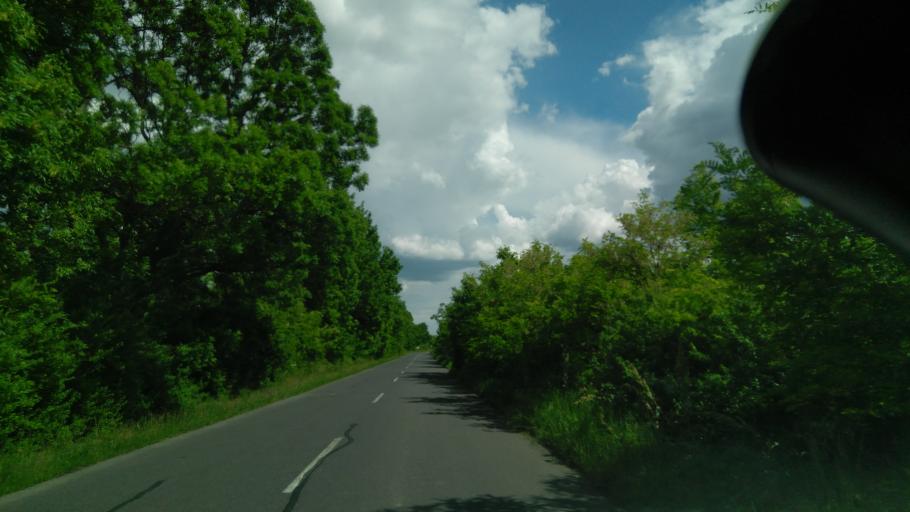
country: HU
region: Bekes
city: Korosladany
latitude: 46.9797
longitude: 21.0522
